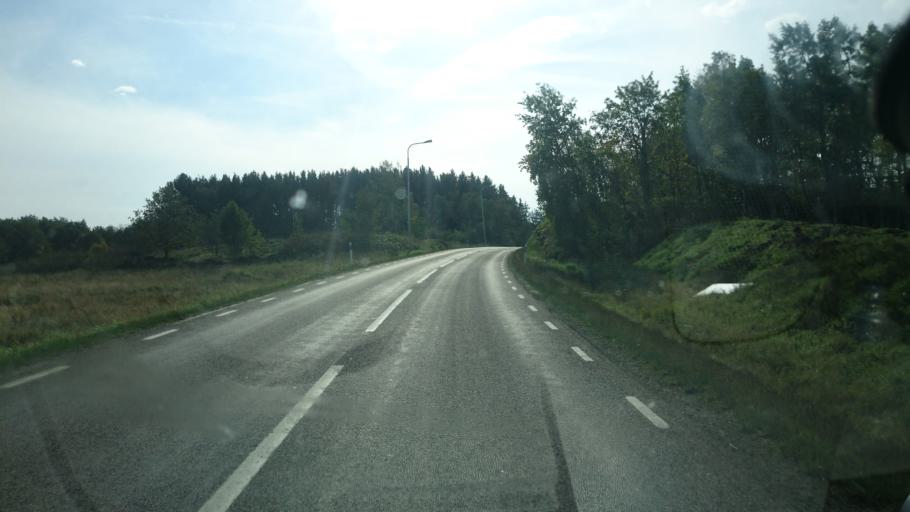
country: SE
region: Vaestra Goetaland
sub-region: Vanersborgs Kommun
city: Vargon
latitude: 58.2479
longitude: 12.4226
